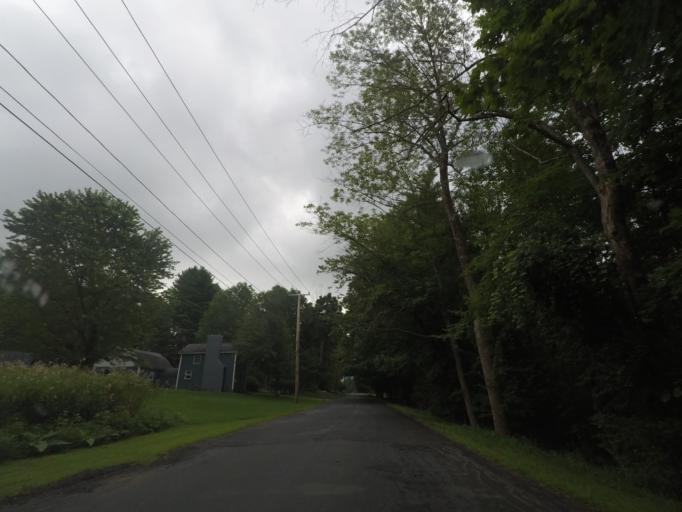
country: US
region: Massachusetts
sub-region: Berkshire County
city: Richmond
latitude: 42.4282
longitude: -73.3185
